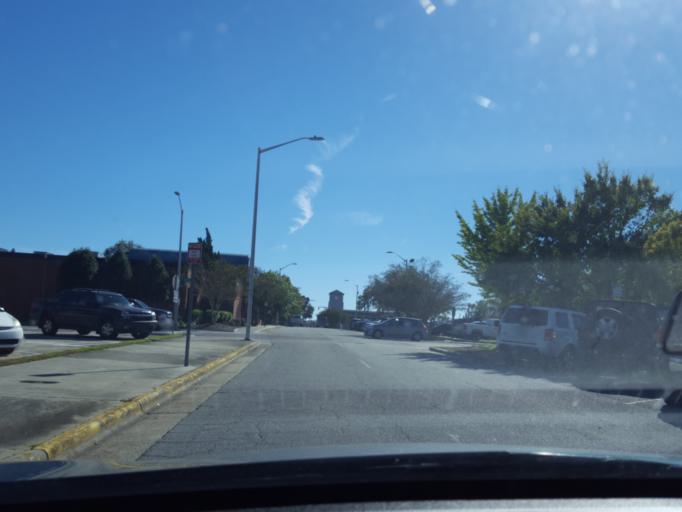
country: US
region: North Carolina
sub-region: Pitt County
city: Greenville
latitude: 35.6145
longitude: -77.3712
